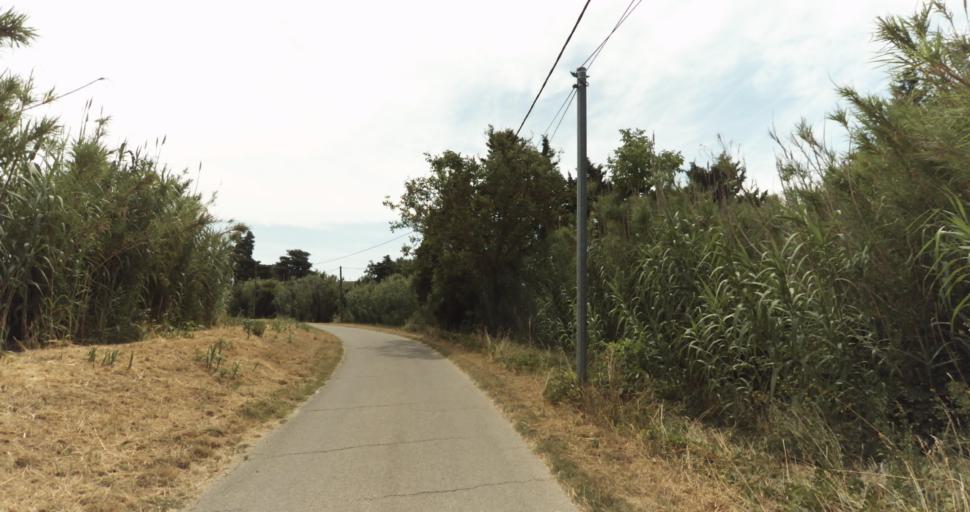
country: FR
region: Provence-Alpes-Cote d'Azur
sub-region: Departement du Vaucluse
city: Monteux
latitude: 44.0505
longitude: 4.9888
